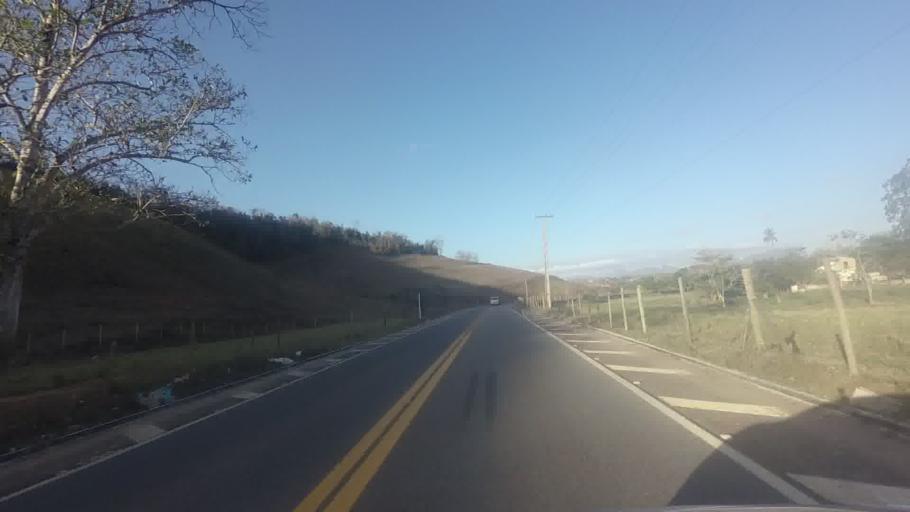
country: BR
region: Espirito Santo
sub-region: Cachoeiro De Itapemirim
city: Cachoeiro de Itapemirim
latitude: -20.8267
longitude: -41.1885
